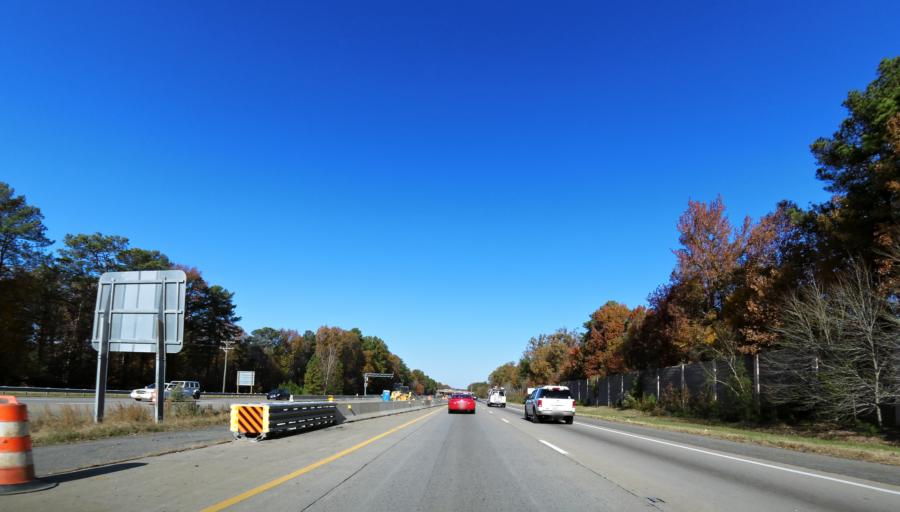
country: US
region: Virginia
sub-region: York County
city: Yorktown
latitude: 37.1304
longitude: -76.5219
